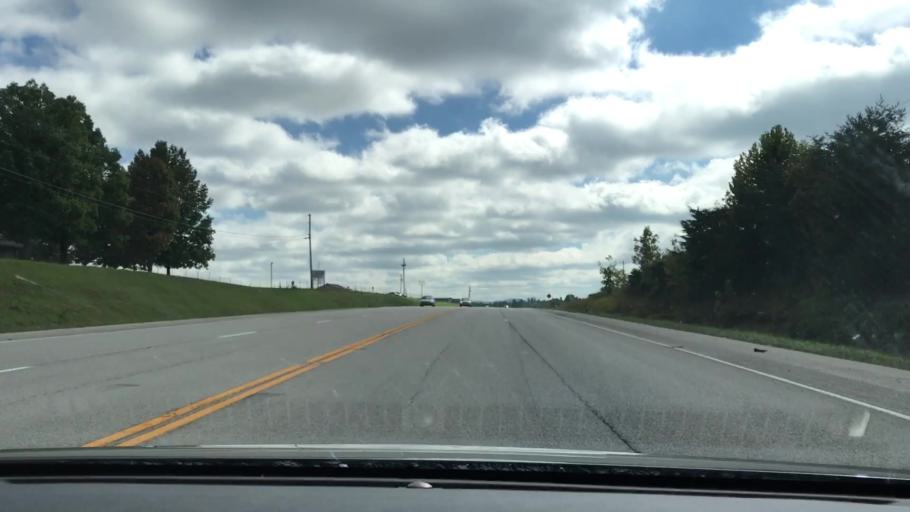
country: US
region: Kentucky
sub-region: McCreary County
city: Pine Knot
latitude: 36.6453
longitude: -84.4337
